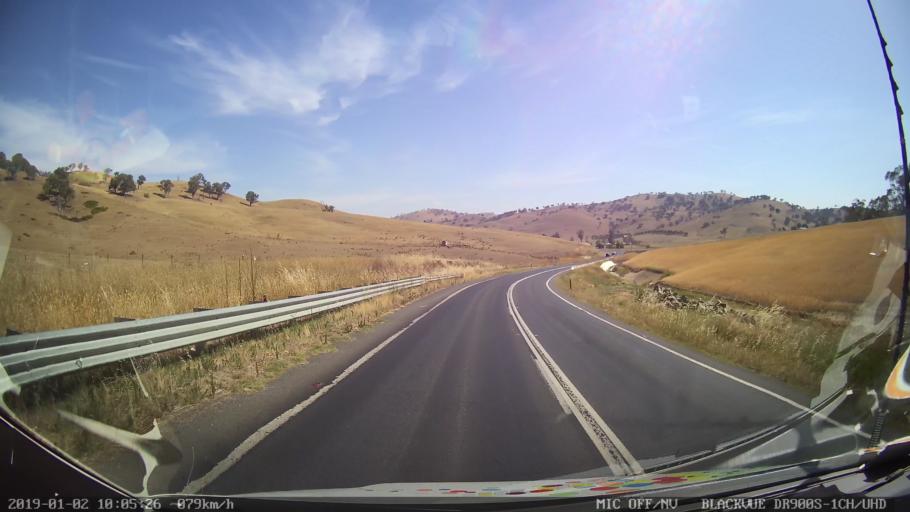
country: AU
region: New South Wales
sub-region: Gundagai
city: Gundagai
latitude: -35.1597
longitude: 148.1172
